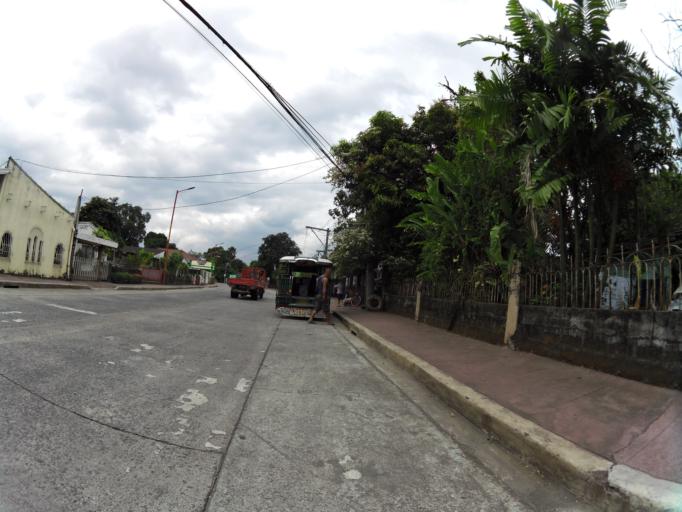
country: PH
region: Calabarzon
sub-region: Province of Rizal
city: Antipolo
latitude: 14.6389
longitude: 121.1163
